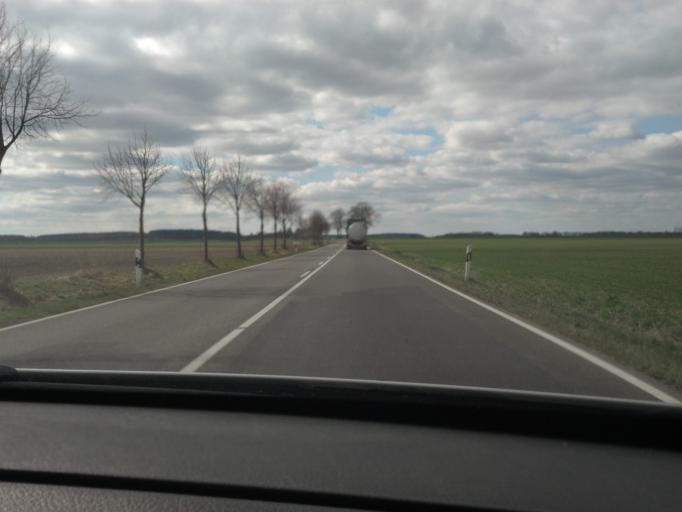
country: DE
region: Mecklenburg-Vorpommern
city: Rechlin
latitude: 53.3311
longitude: 12.6779
